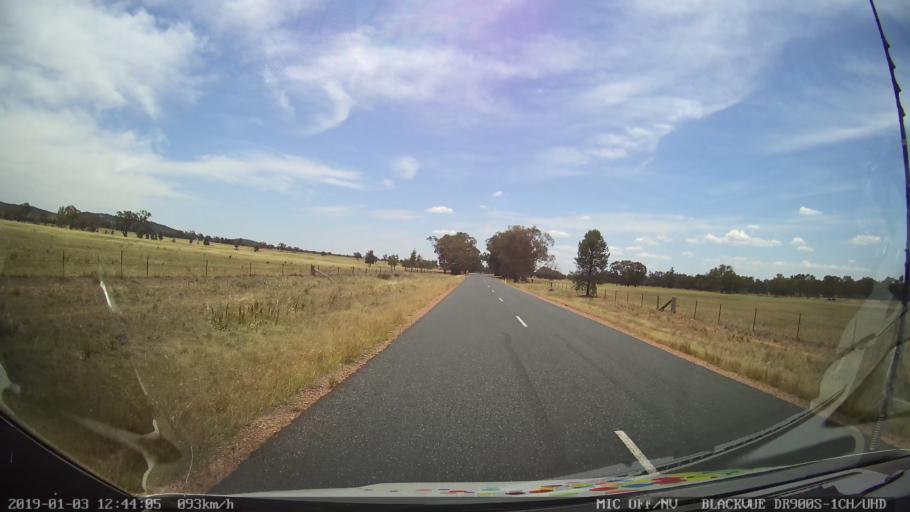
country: AU
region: New South Wales
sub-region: Weddin
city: Grenfell
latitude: -33.7663
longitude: 148.2148
